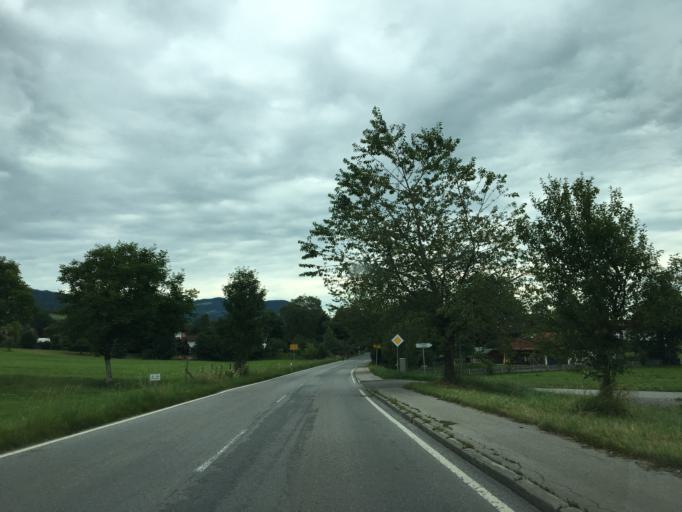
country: DE
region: Bavaria
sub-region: Upper Bavaria
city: Bad Feilnbach
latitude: 47.7618
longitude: 12.0443
